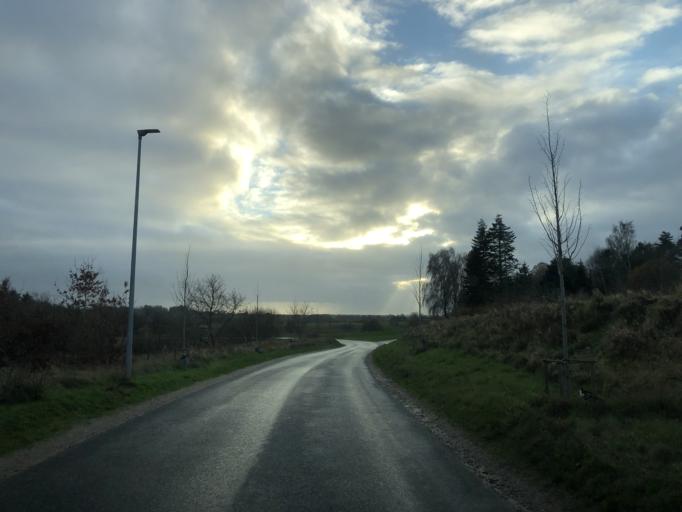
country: DK
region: Central Jutland
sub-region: Viborg Kommune
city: Viborg
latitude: 56.4775
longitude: 9.3415
